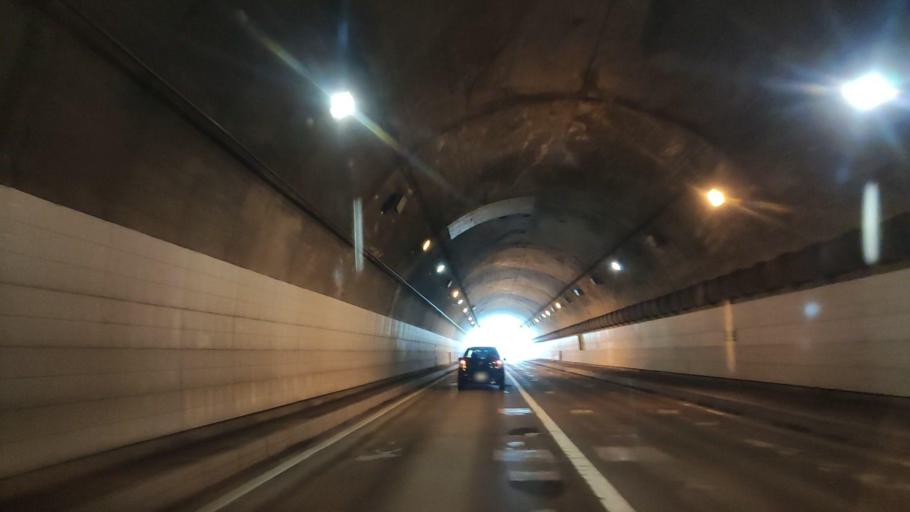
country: JP
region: Akita
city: Takanosu
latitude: 40.2115
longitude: 140.2148
